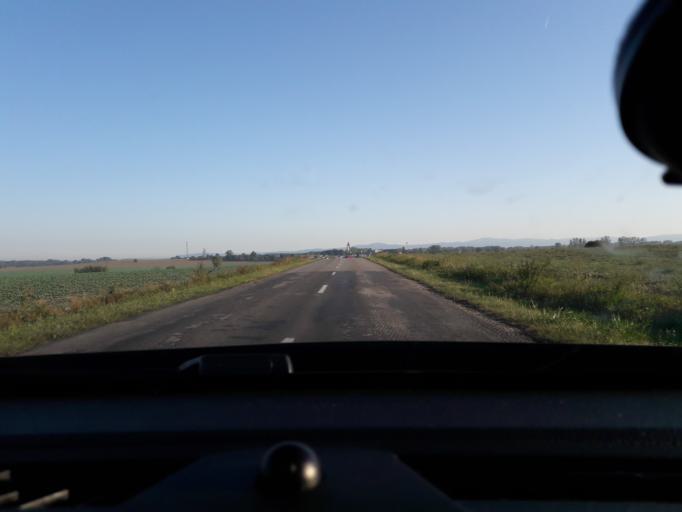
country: SK
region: Kosicky
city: Michalovce
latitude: 48.5805
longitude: 21.9673
